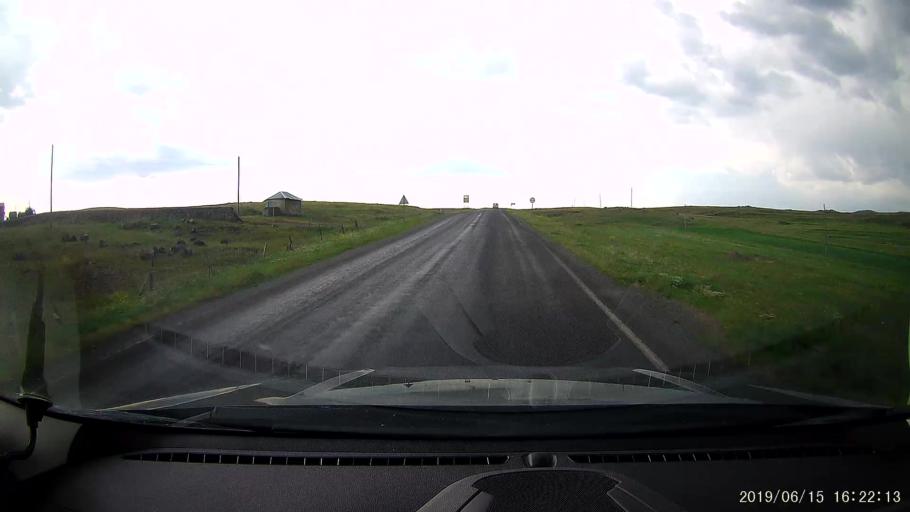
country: TR
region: Ardahan
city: Hanak
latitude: 41.1901
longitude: 42.8483
